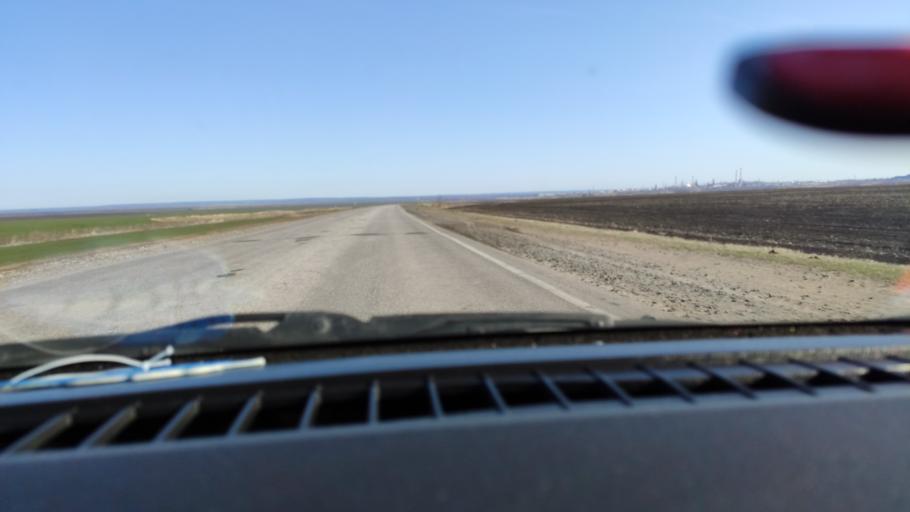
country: RU
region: Samara
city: Varlamovo
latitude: 53.0284
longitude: 48.3343
